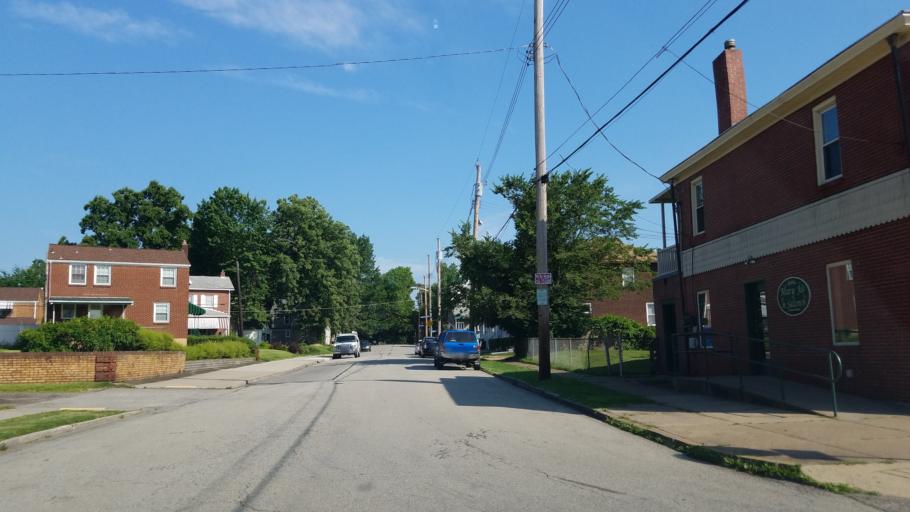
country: US
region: Pennsylvania
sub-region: Allegheny County
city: Swissvale
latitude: 40.4219
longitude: -79.8978
